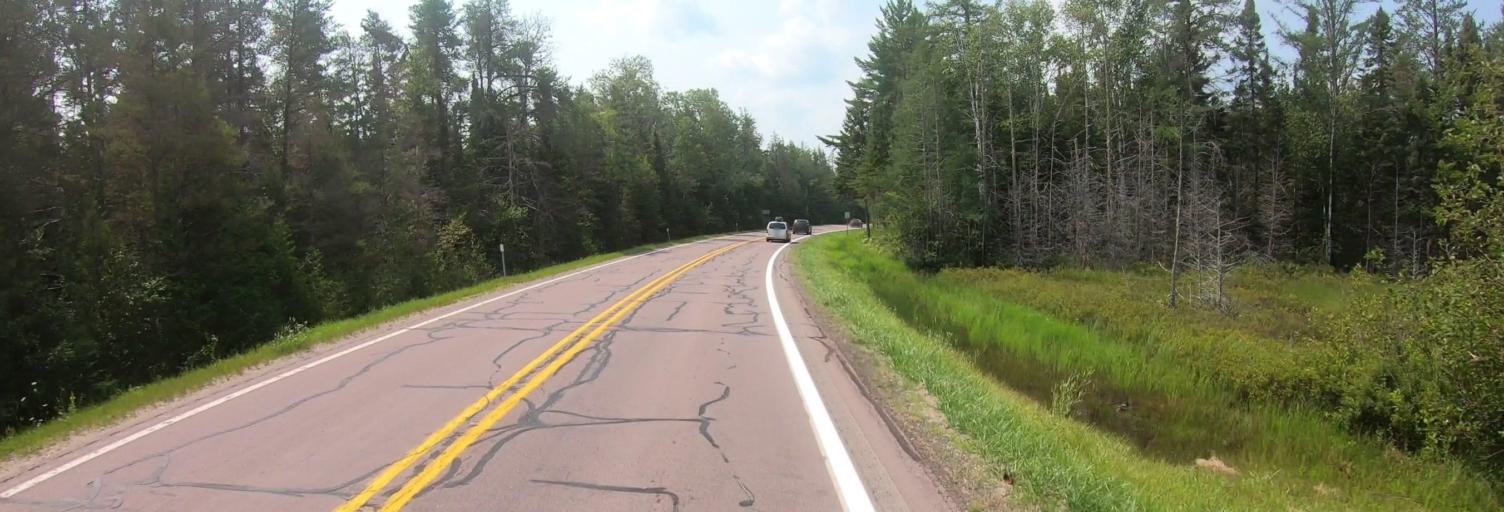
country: US
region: Michigan
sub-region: Luce County
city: Newberry
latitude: 46.4731
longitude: -85.4271
